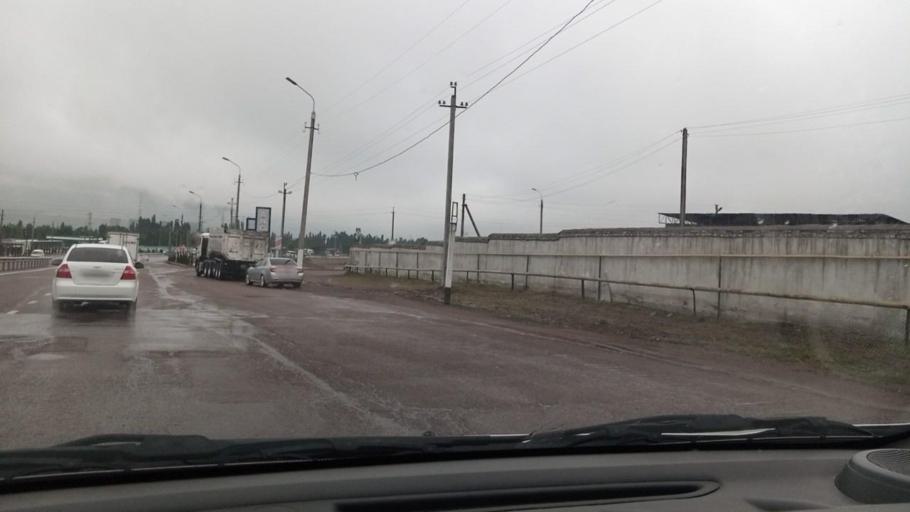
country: UZ
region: Toshkent
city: Angren
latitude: 41.0290
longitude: 70.1371
